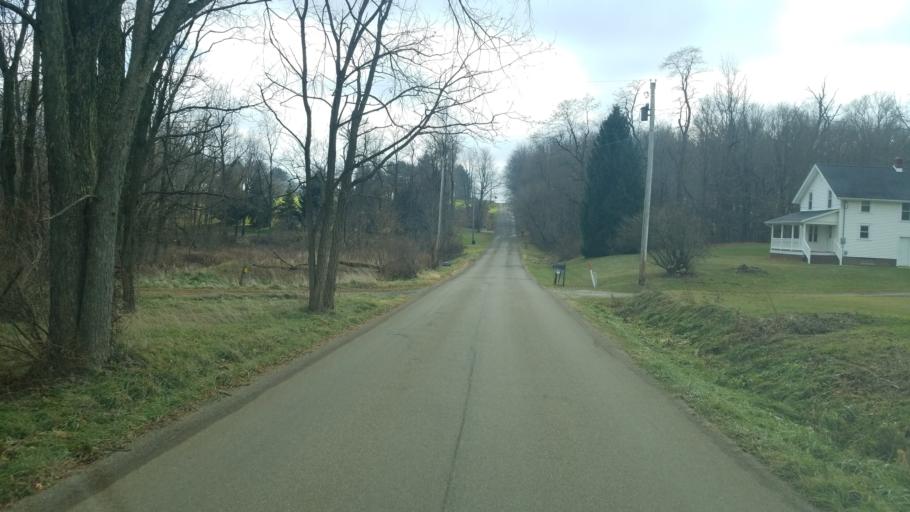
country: US
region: Ohio
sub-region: Richland County
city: Lincoln Heights
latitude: 40.8100
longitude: -82.4749
